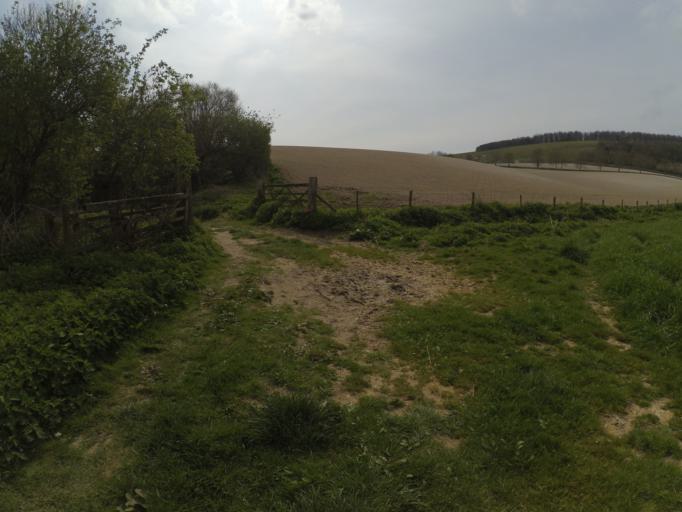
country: GB
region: England
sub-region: West Sussex
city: Arundel
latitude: 50.8796
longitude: -0.5502
